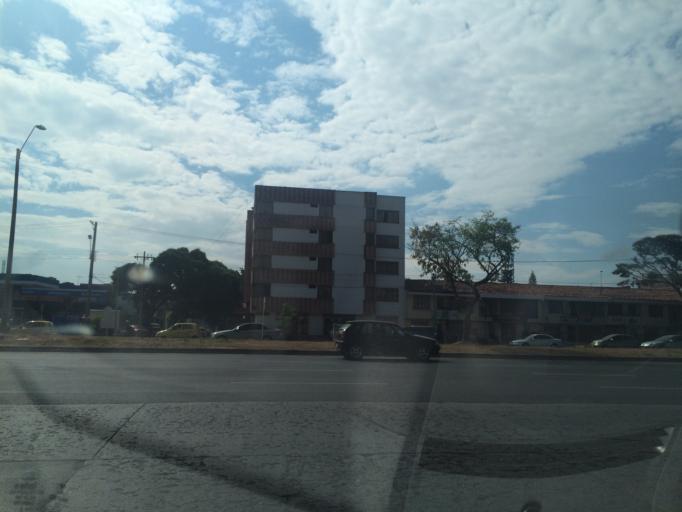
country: CO
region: Valle del Cauca
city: Cali
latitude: 3.4144
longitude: -76.5377
